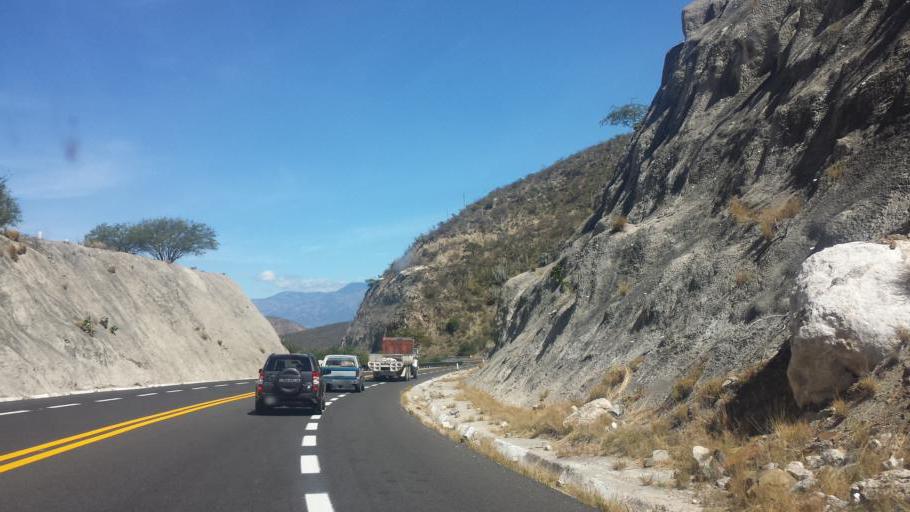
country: MX
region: Puebla
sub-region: San Jose Miahuatlan
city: San Pedro Tetitlan
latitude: 18.1382
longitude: -97.3195
